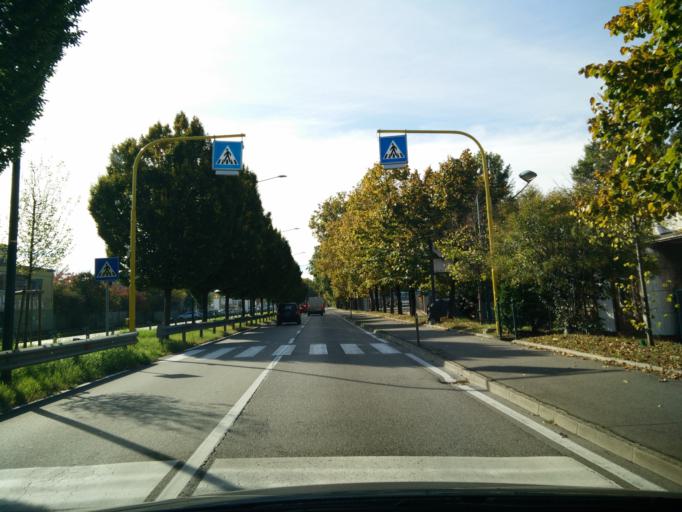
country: IT
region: Veneto
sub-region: Provincia di Venezia
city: Mestre
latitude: 45.4699
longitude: 12.2281
